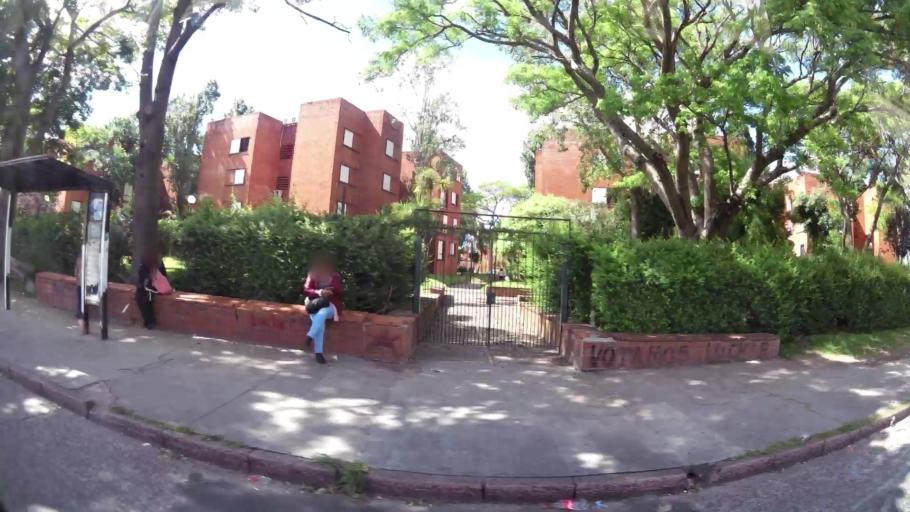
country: UY
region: Canelones
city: Paso de Carrasco
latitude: -34.8725
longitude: -56.1217
